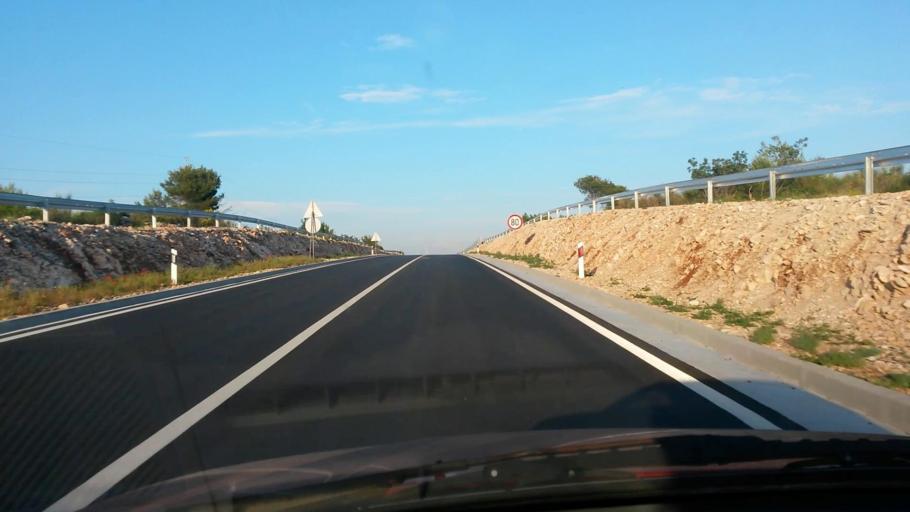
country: HR
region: Sibensko-Kniniska
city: Vodice
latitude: 43.7752
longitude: 15.7761
